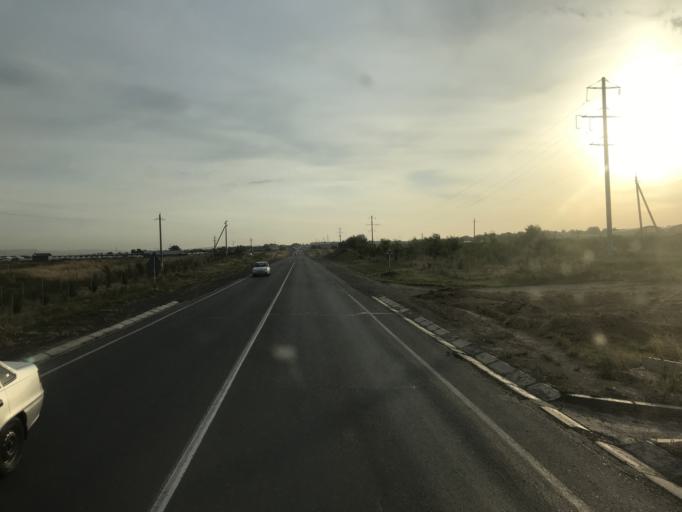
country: KZ
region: Ongtustik Qazaqstan
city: Saryaghash
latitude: 41.4461
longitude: 69.1279
